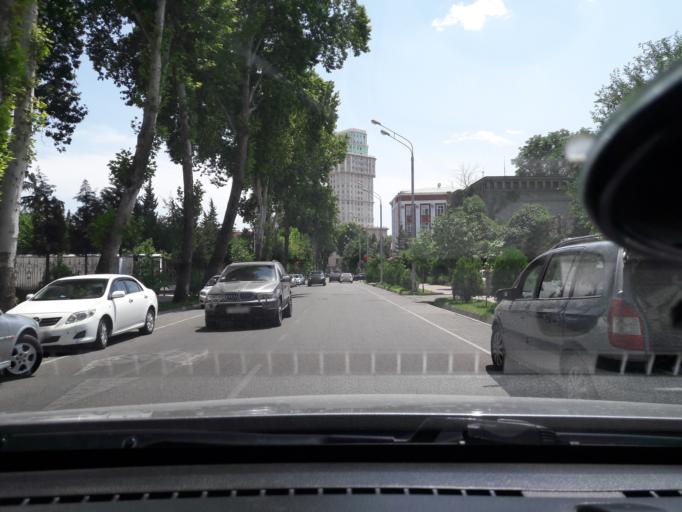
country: TJ
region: Dushanbe
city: Dushanbe
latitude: 38.5754
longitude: 68.7894
